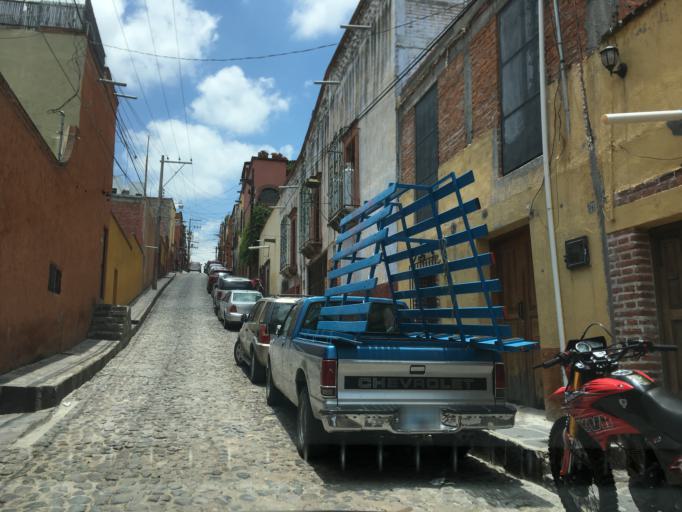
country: MX
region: Guanajuato
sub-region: San Miguel de Allende
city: San Miguel de Allende
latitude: 20.9140
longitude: -100.7483
